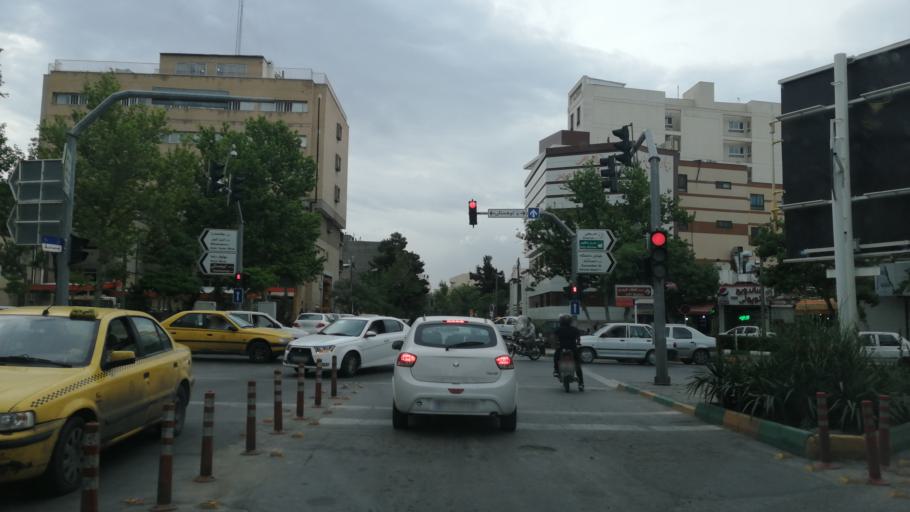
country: IR
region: Razavi Khorasan
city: Mashhad
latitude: 36.2880
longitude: 59.5777
